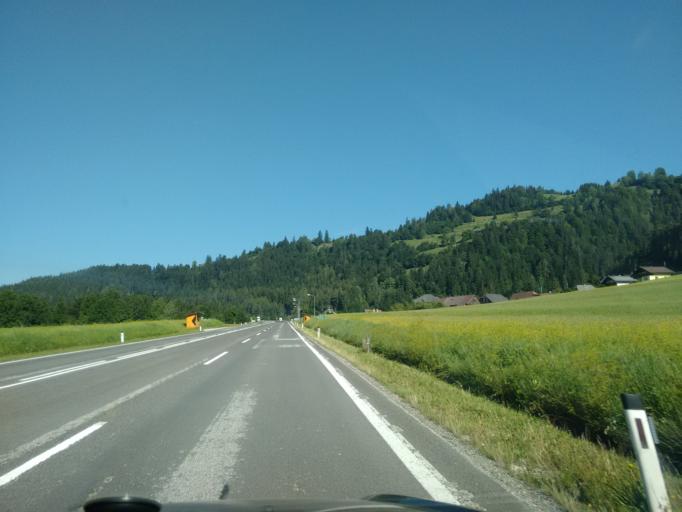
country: AT
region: Styria
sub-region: Politischer Bezirk Liezen
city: Tauplitz
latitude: 47.5427
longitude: 14.0433
